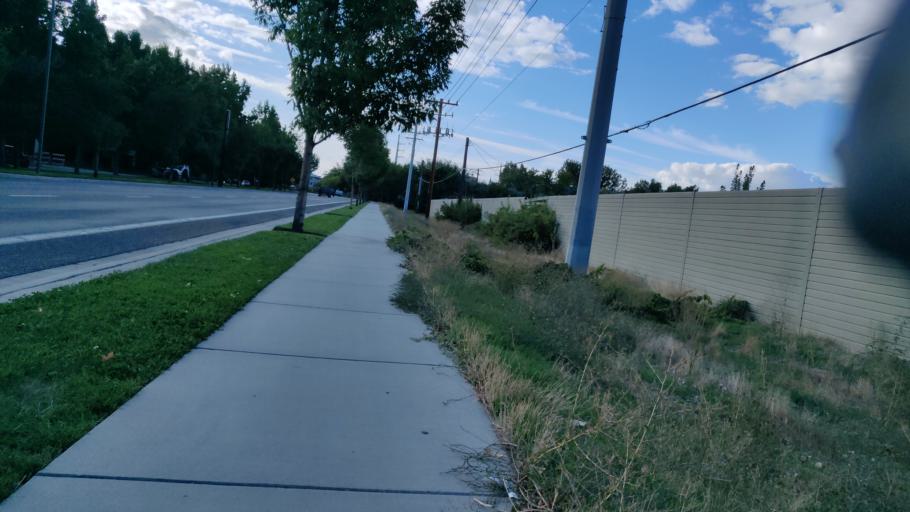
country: US
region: Idaho
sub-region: Ada County
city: Boise
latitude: 43.6060
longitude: -116.1885
